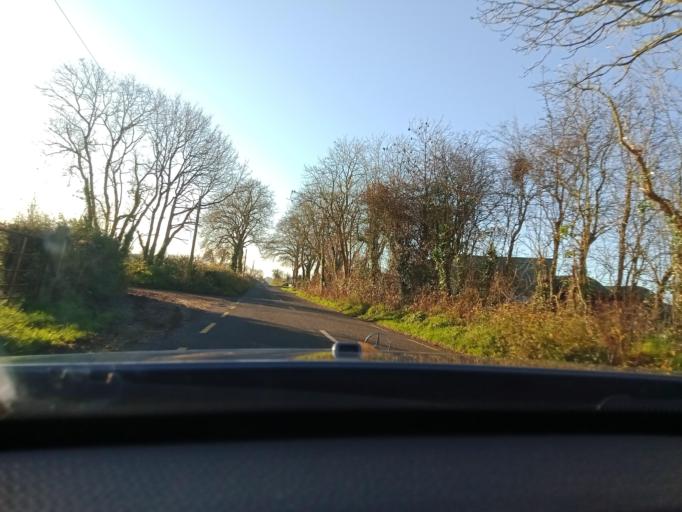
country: IE
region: Leinster
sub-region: Kilkenny
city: Callan
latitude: 52.4883
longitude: -7.3855
